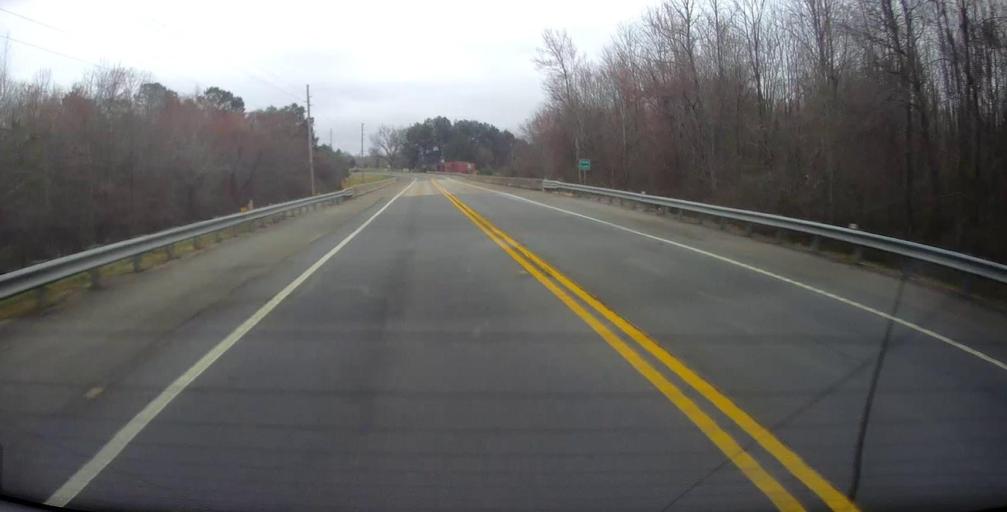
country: US
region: Georgia
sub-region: Pike County
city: Zebulon
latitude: 33.1037
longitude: -84.3621
